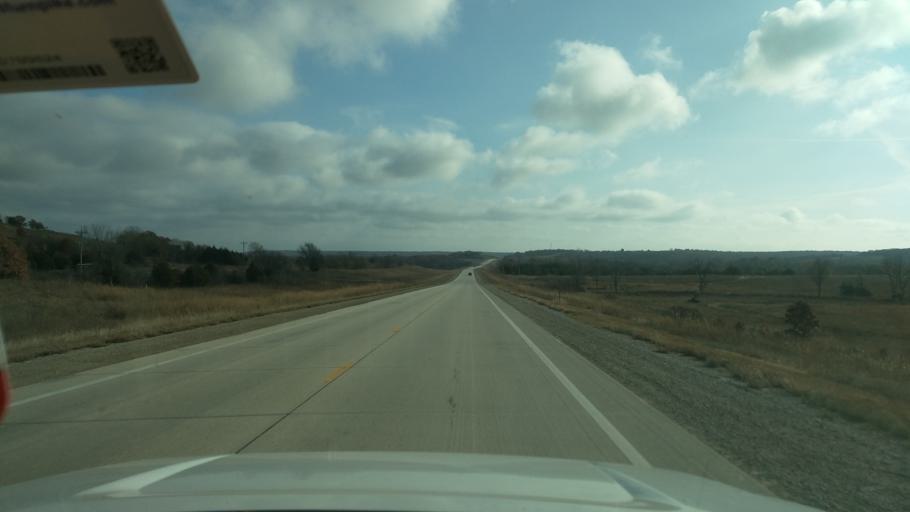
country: US
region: Kansas
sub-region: Chautauqua County
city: Sedan
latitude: 37.0828
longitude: -96.1366
